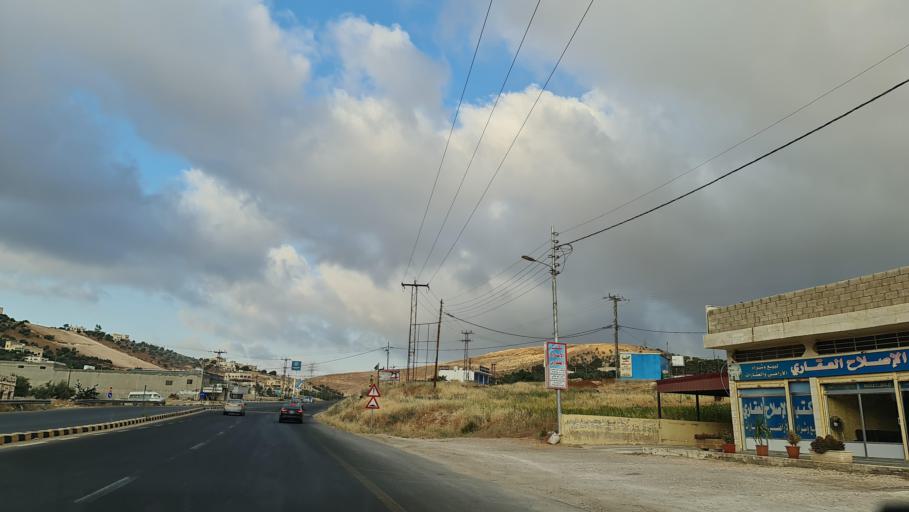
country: JO
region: Amman
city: Al Jubayhah
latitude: 32.0920
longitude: 35.9368
